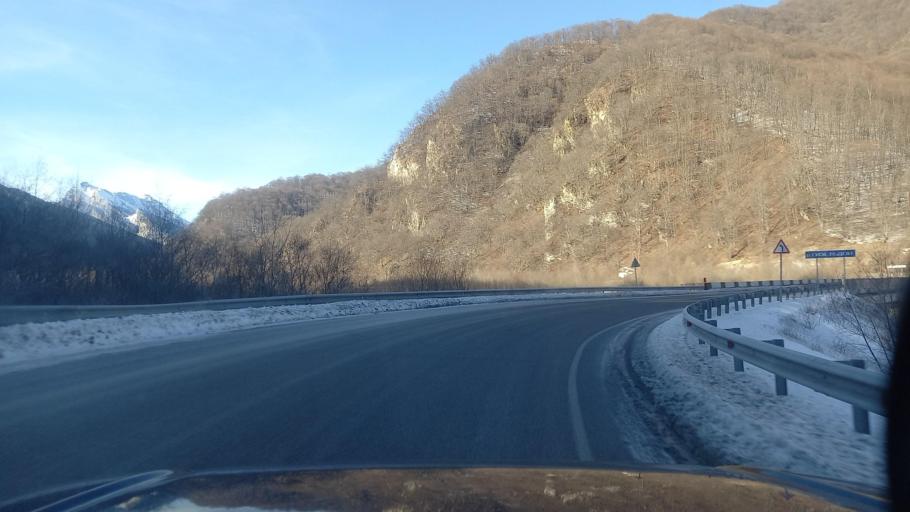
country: RU
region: North Ossetia
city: Gizel'
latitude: 42.9315
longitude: 44.5487
